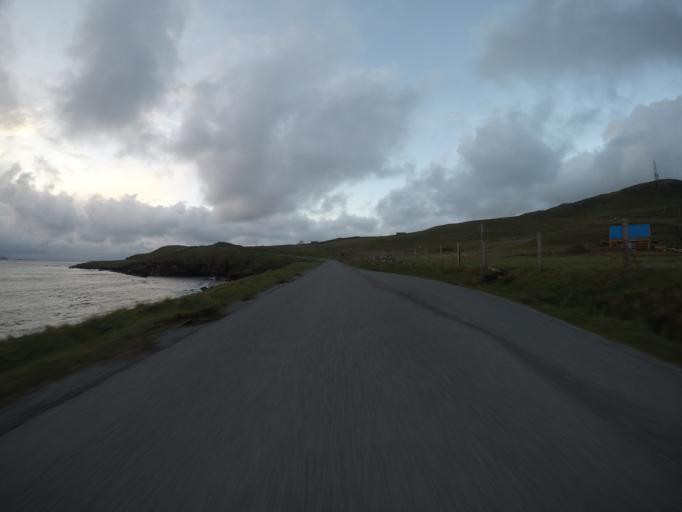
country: GB
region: Scotland
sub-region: Highland
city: Portree
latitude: 57.6792
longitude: -6.3450
